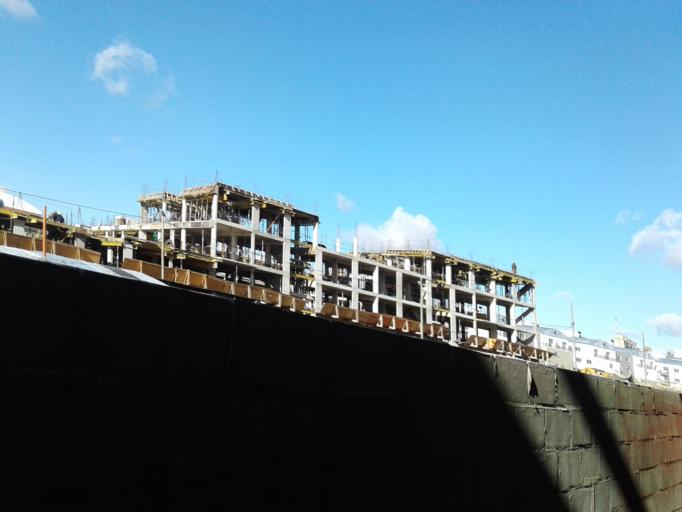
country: AR
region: Buenos Aires F.D.
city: Villa Lugano
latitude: -34.6747
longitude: -58.4636
